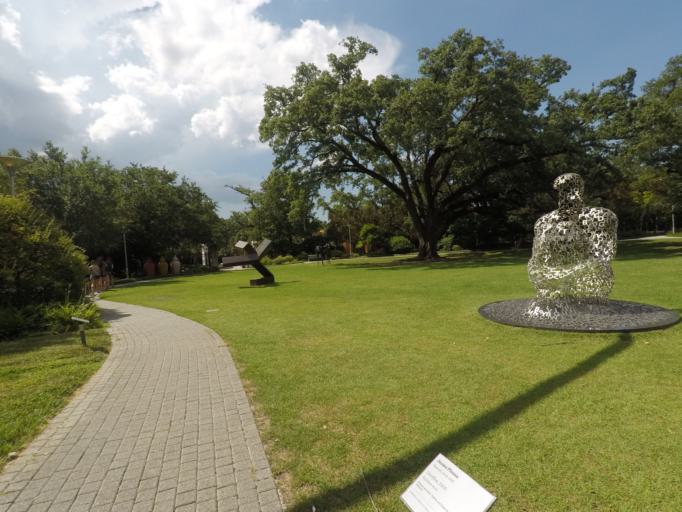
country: US
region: Louisiana
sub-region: Orleans Parish
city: New Orleans
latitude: 29.9864
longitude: -90.0953
